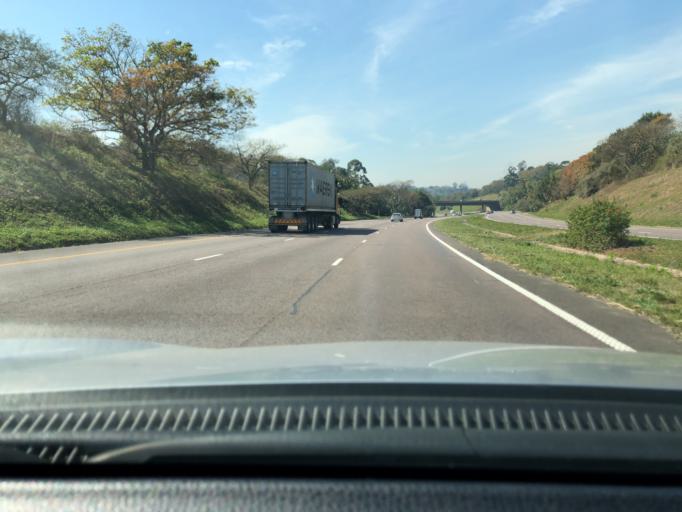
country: ZA
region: KwaZulu-Natal
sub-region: eThekwini Metropolitan Municipality
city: Berea
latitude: -29.8337
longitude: 30.8837
